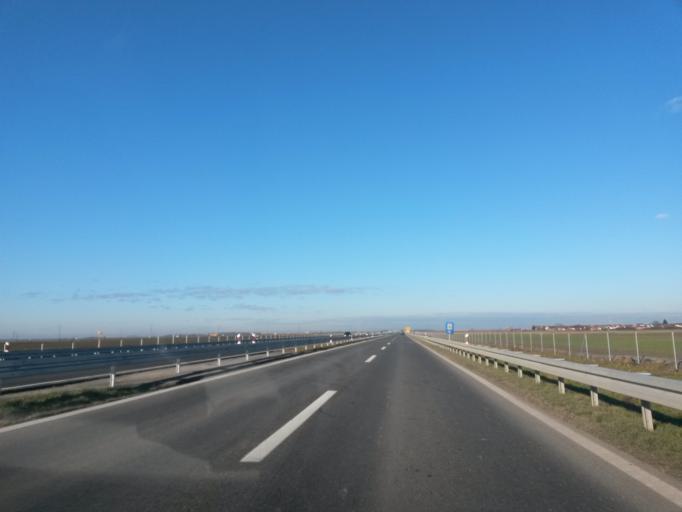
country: HR
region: Osjecko-Baranjska
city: Josipovac
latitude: 45.5648
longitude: 18.5915
